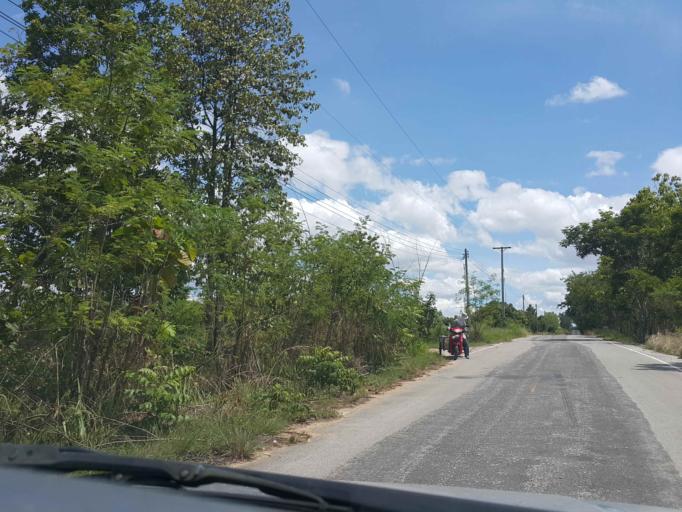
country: TH
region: Chiang Mai
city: Doi Lo
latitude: 18.5068
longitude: 98.7642
